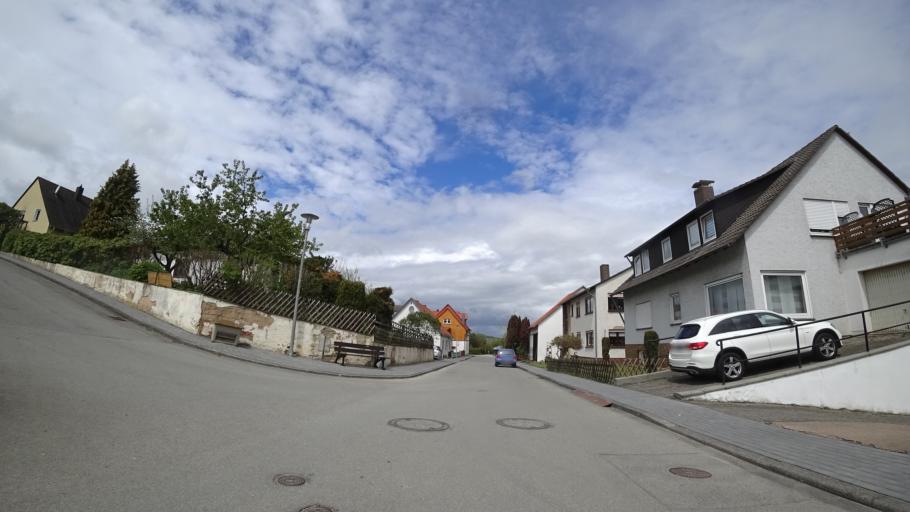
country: DE
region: Hesse
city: Liebenau
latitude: 51.4578
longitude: 9.3122
